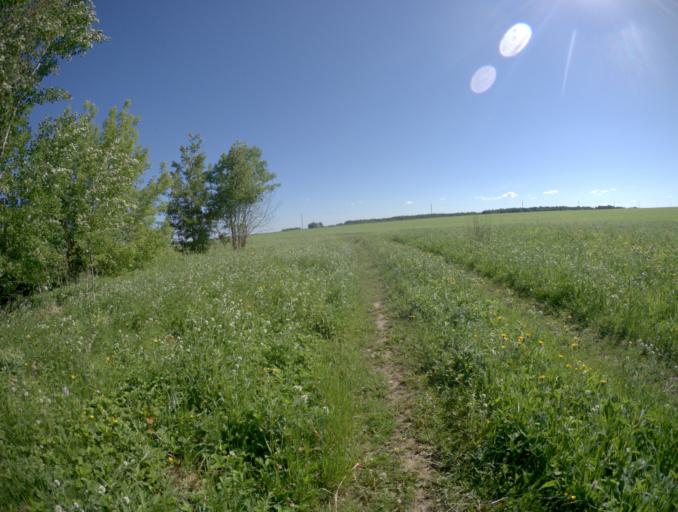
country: RU
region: Ivanovo
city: Gavrilov Posad
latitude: 56.5413
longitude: 40.1993
